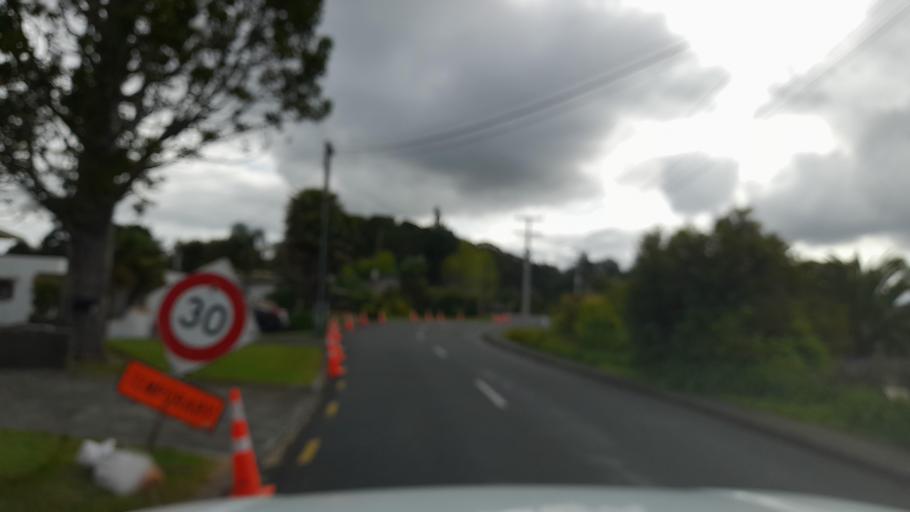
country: NZ
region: Northland
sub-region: Whangarei
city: Whangarei
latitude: -35.7395
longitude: 174.3188
